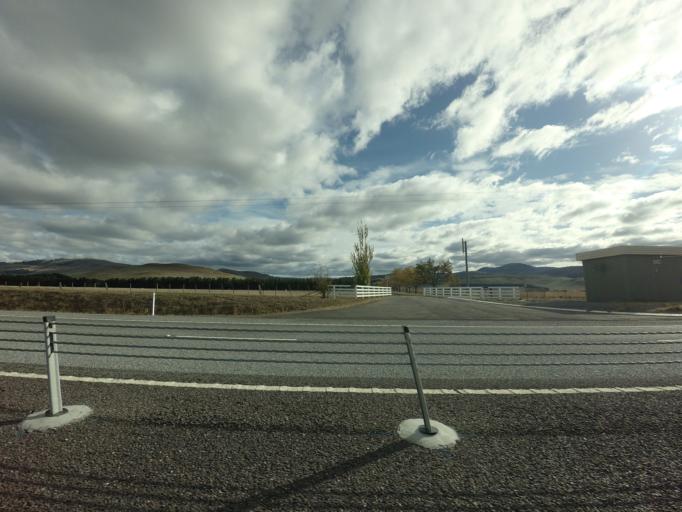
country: AU
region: Tasmania
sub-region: Brighton
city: Bridgewater
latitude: -42.5027
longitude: 147.1873
